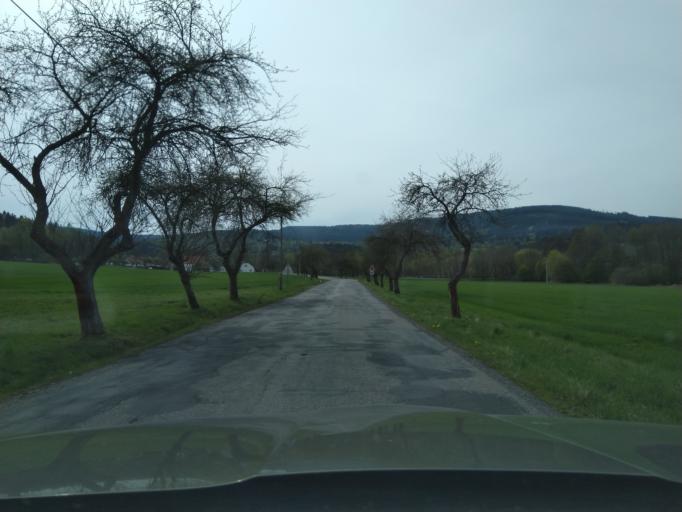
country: CZ
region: Plzensky
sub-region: Okres Klatovy
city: Kasperske Hory
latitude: 49.1822
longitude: 13.6285
